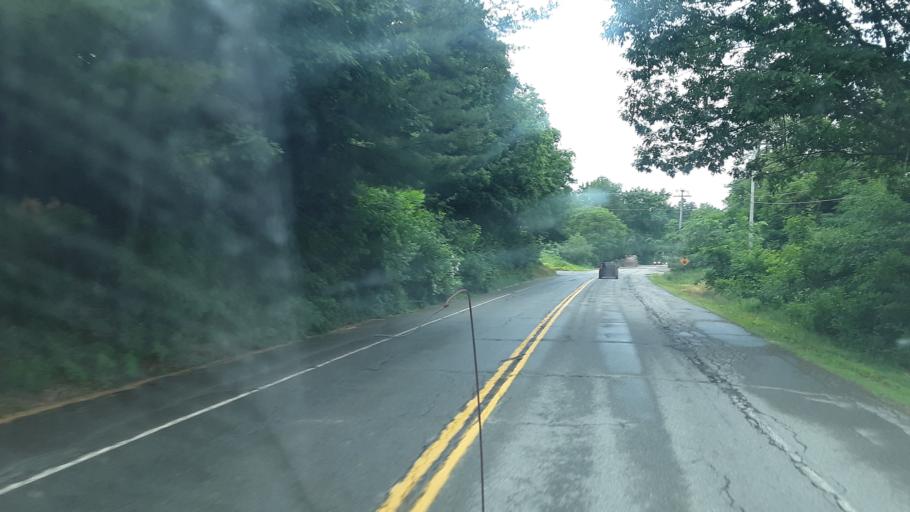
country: US
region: Maine
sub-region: Penobscot County
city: Eddington
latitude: 44.8276
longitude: -68.6939
